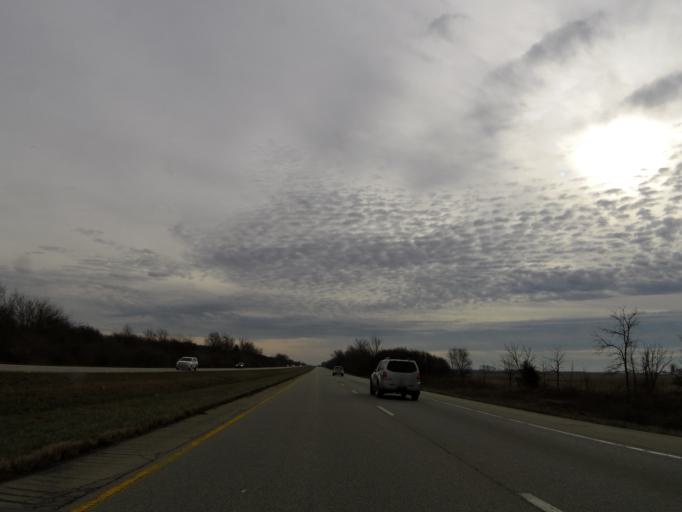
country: US
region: Indiana
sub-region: Boone County
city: Thorntown
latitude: 39.9894
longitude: -86.7045
